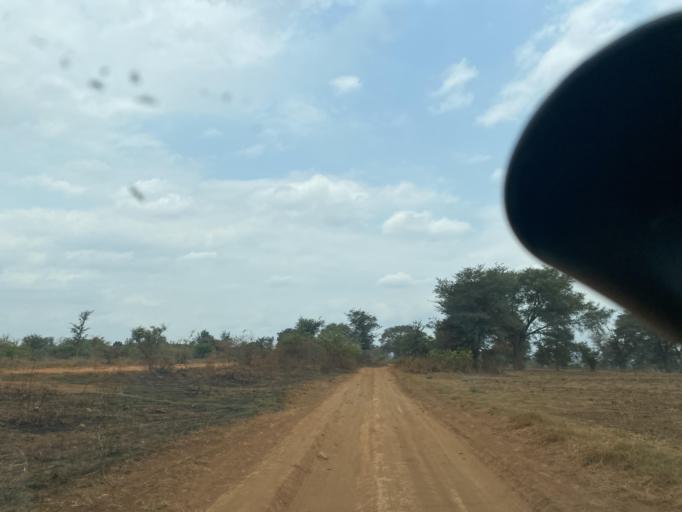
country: ZM
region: Lusaka
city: Chongwe
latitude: -15.5010
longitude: 28.8077
